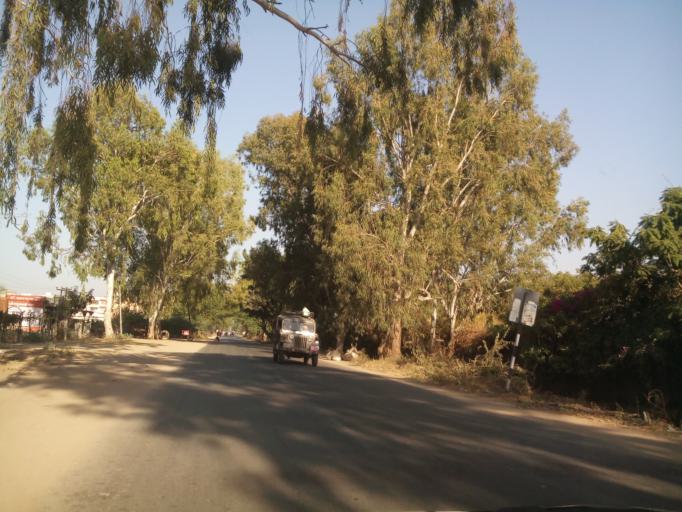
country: IN
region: Rajasthan
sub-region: Sirohi
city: Abu Road
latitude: 24.5353
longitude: 72.7975
